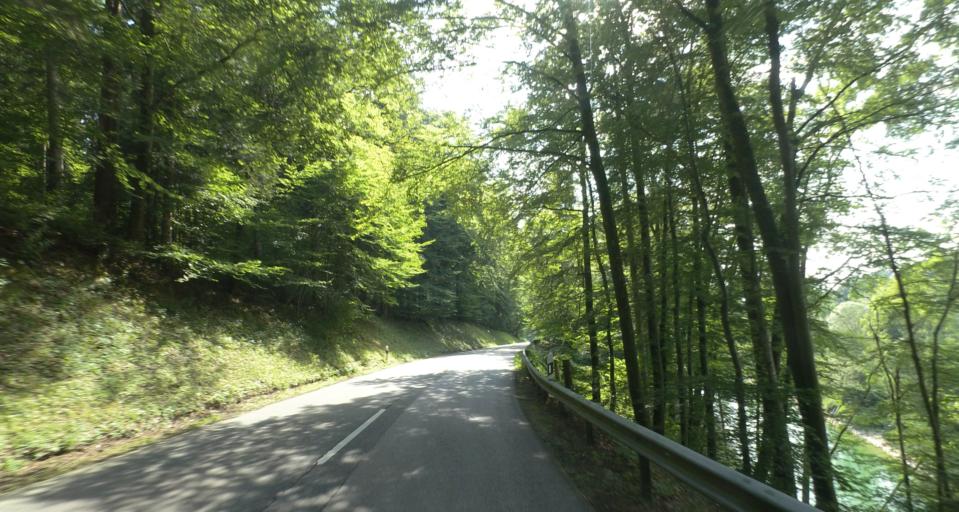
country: DE
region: Bavaria
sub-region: Upper Bavaria
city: Seeon-Seebruck
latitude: 47.9627
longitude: 12.5118
